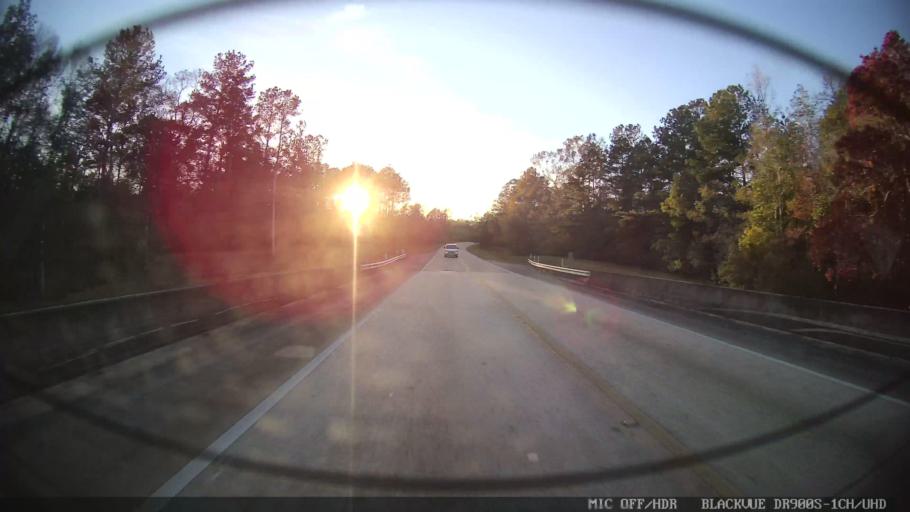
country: US
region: Mississippi
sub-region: Lamar County
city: Lumberton
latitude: 30.9944
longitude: -89.3780
